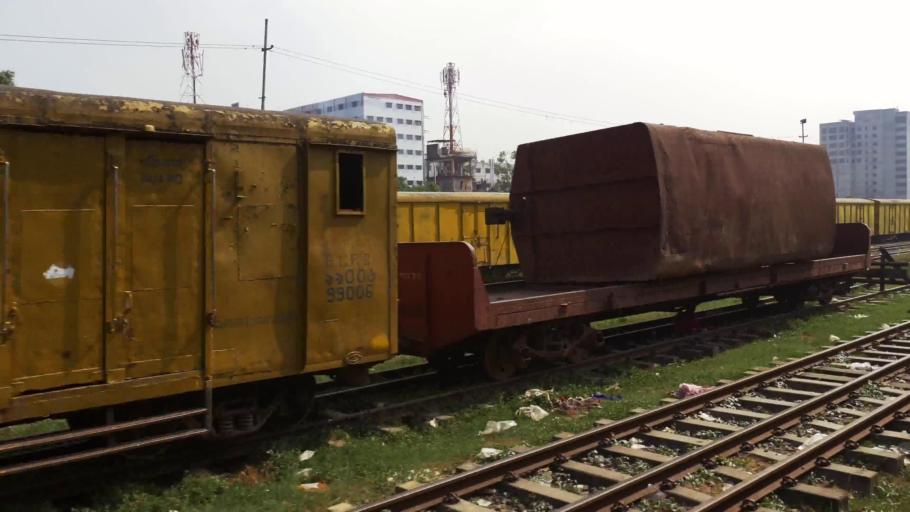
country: BD
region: Dhaka
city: Paltan
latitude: 23.7975
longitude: 90.4010
